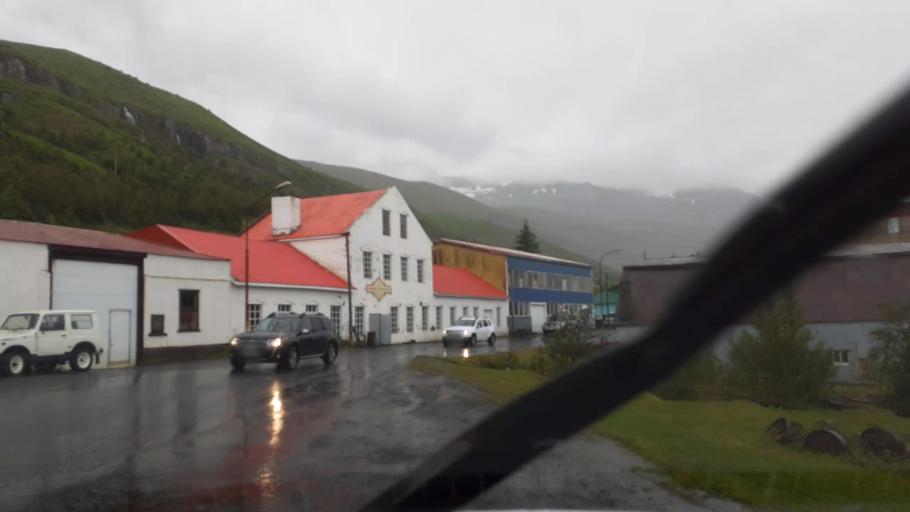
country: IS
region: East
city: Eskifjoerdur
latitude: 65.2657
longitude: -13.9919
